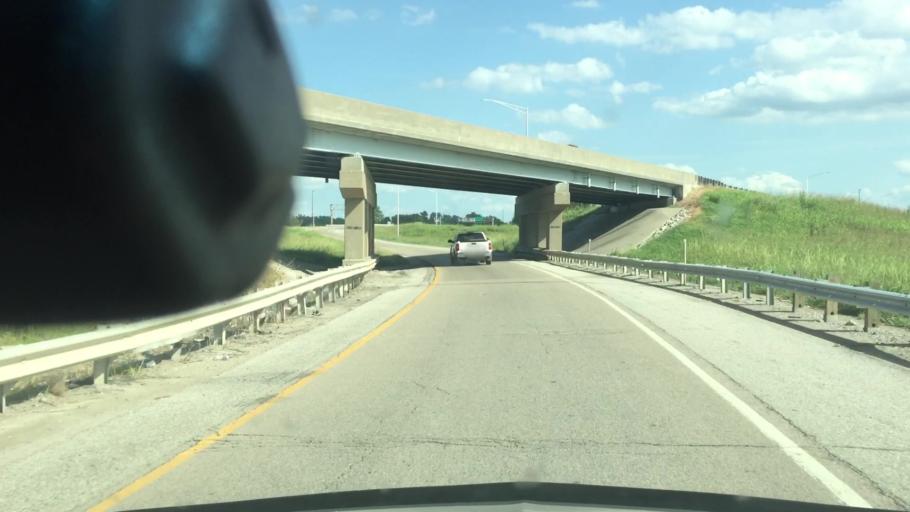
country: US
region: Illinois
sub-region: Saint Clair County
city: East Saint Louis
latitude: 38.6481
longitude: -90.1320
